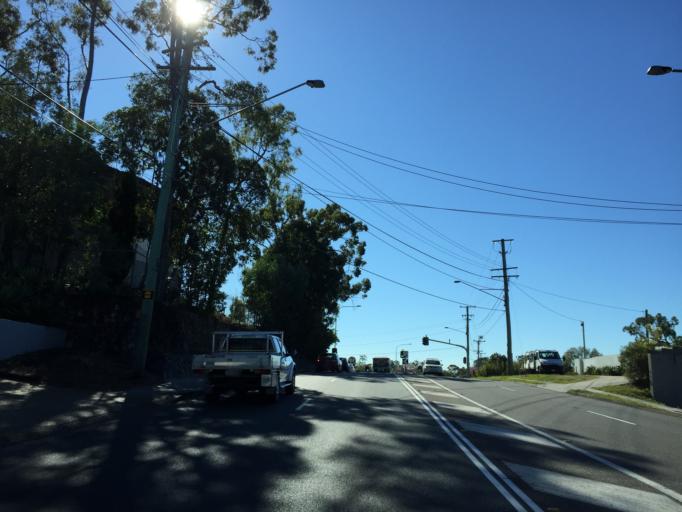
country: AU
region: Queensland
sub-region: Brisbane
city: Everton Park
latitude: -27.4125
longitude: 152.9619
